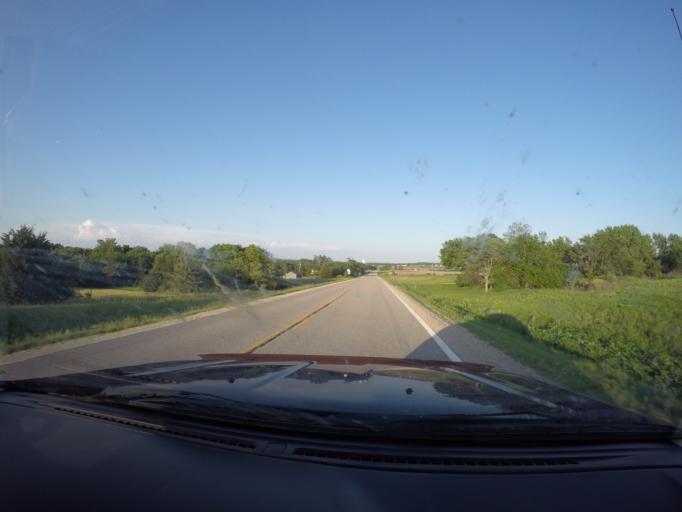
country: US
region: Kansas
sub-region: Marshall County
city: Blue Rapids
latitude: 39.6896
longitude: -96.7822
